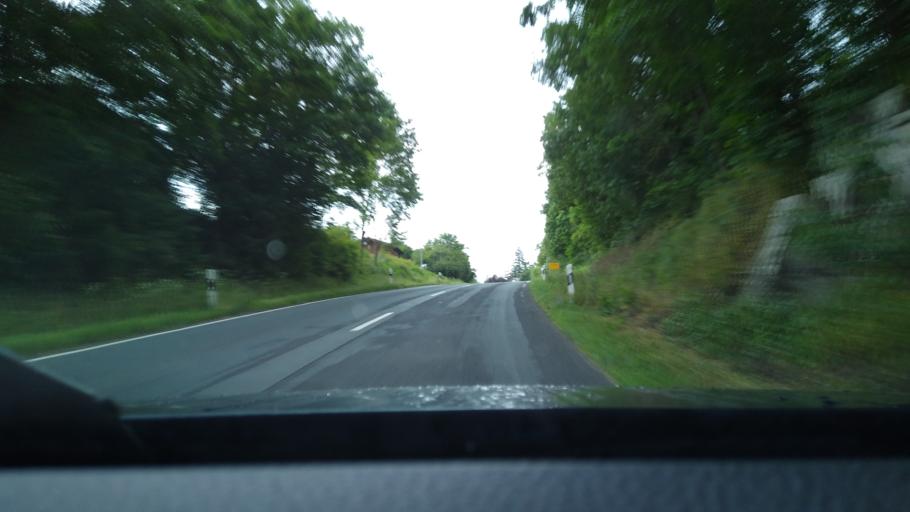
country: DE
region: Bavaria
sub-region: Regierungsbezirk Mittelfranken
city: Trautskirchen
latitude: 49.4586
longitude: 10.5862
